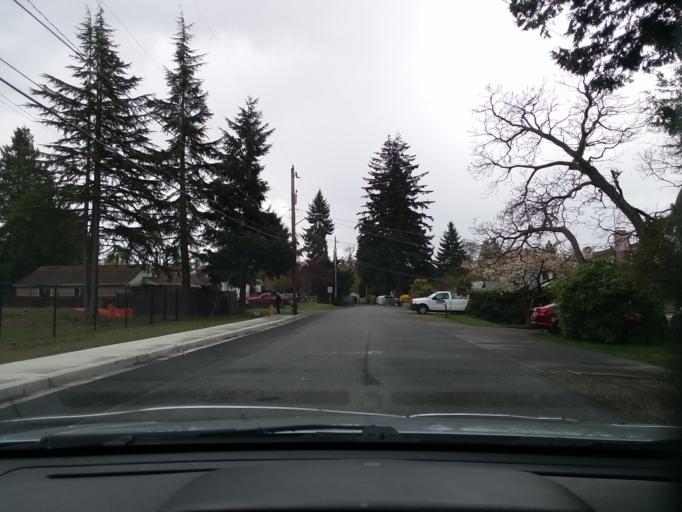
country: US
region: Washington
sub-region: King County
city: Shoreline
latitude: 47.7425
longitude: -122.3144
